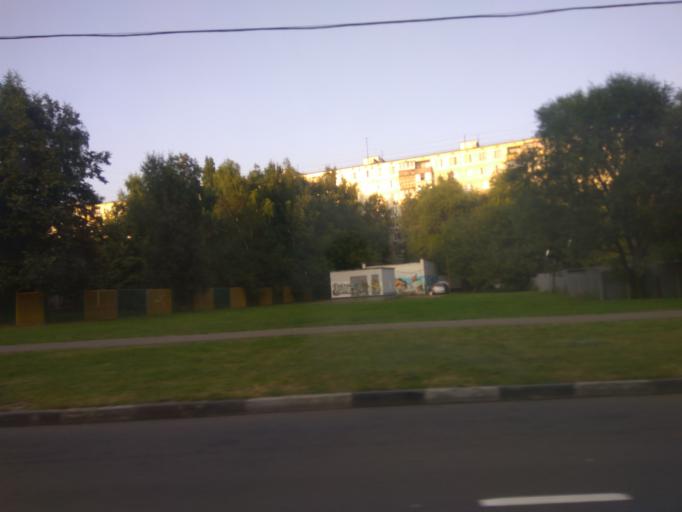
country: RU
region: Moscow
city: Orekhovo-Borisovo
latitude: 55.6069
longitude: 37.7113
